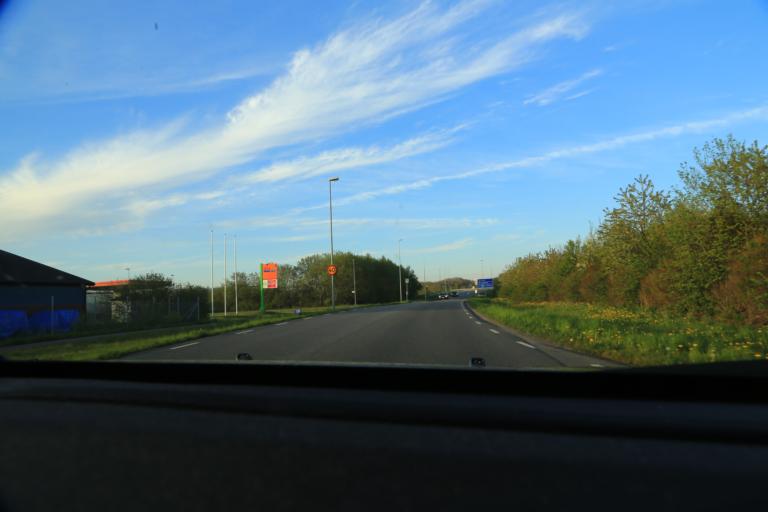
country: SE
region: Halland
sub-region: Varbergs Kommun
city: Traslovslage
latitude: 57.0553
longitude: 12.2959
